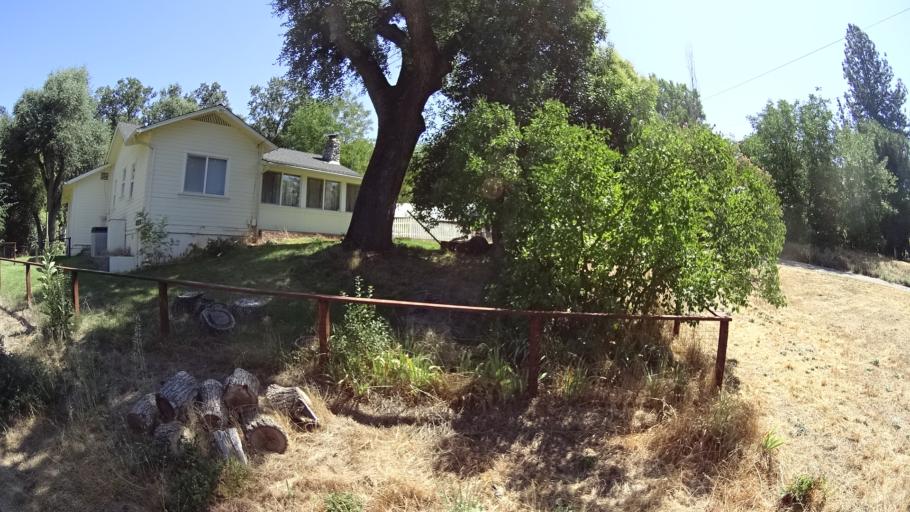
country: US
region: California
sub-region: Calaveras County
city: Angels Camp
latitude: 38.0720
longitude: -120.5355
